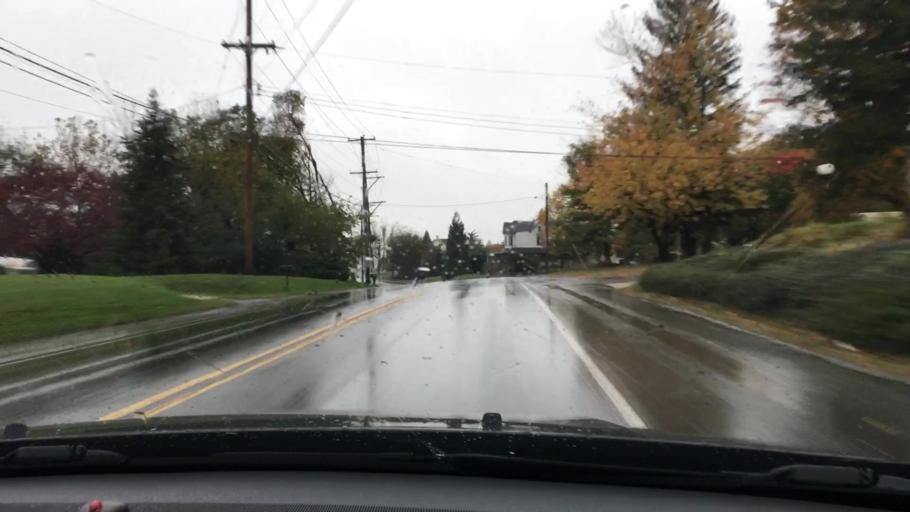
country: US
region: Pennsylvania
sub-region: York County
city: Susquehanna Trails
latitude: 39.8040
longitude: -76.3690
